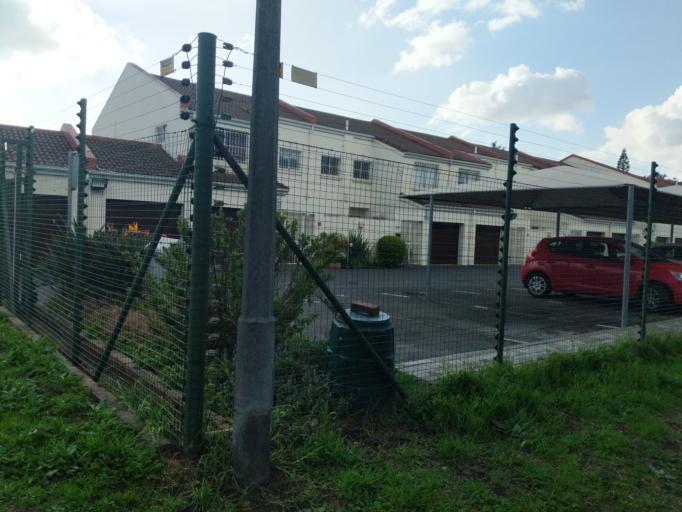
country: ZA
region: Western Cape
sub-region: City of Cape Town
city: Rosebank
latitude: -33.9358
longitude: 18.5119
